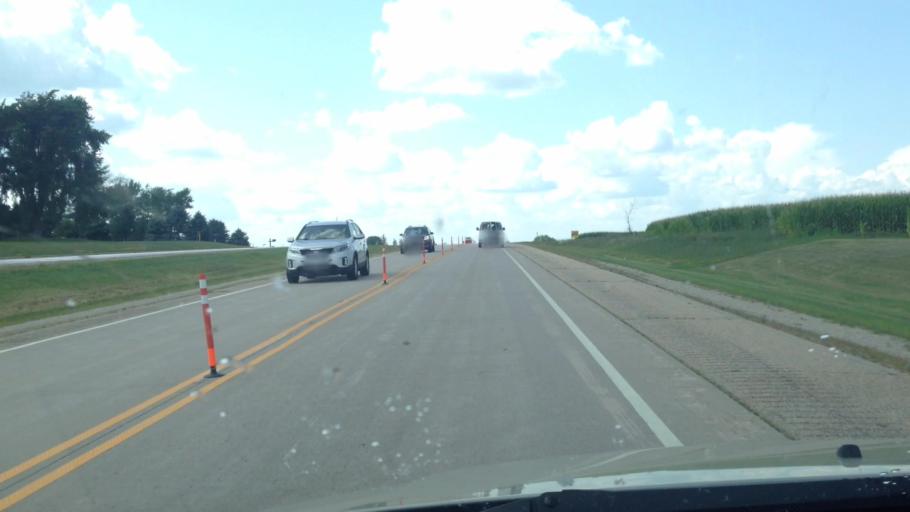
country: US
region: Wisconsin
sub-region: Shawano County
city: Bonduel
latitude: 44.6980
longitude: -88.3537
